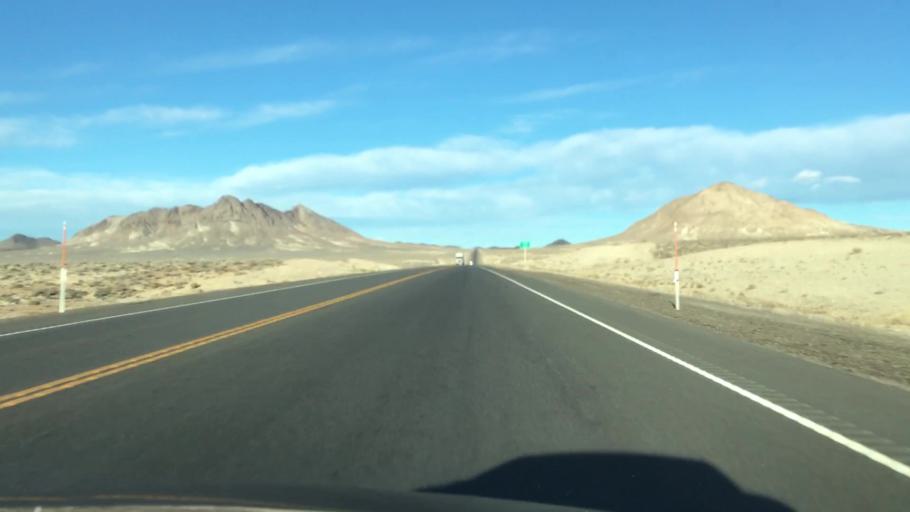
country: US
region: Nevada
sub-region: Nye County
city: Tonopah
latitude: 38.0080
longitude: -117.2592
